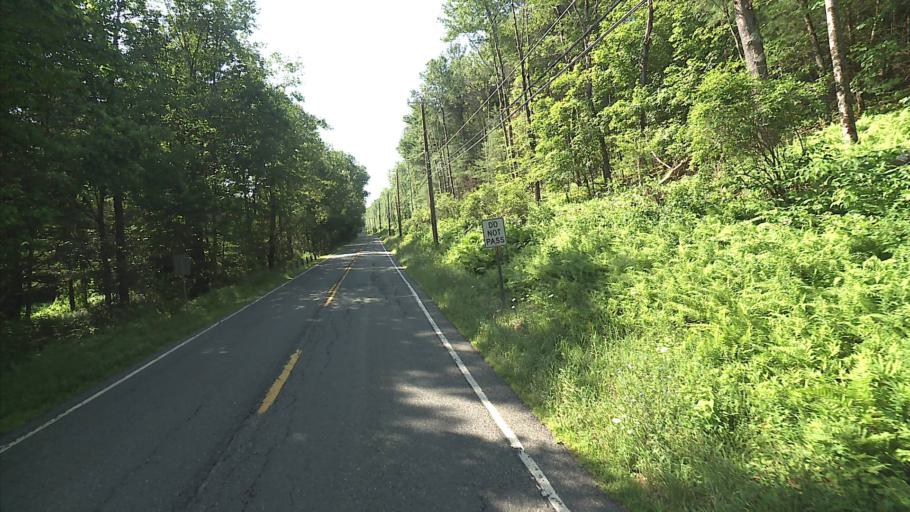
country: US
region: Connecticut
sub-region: Litchfield County
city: Winsted
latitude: 42.0014
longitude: -73.1036
